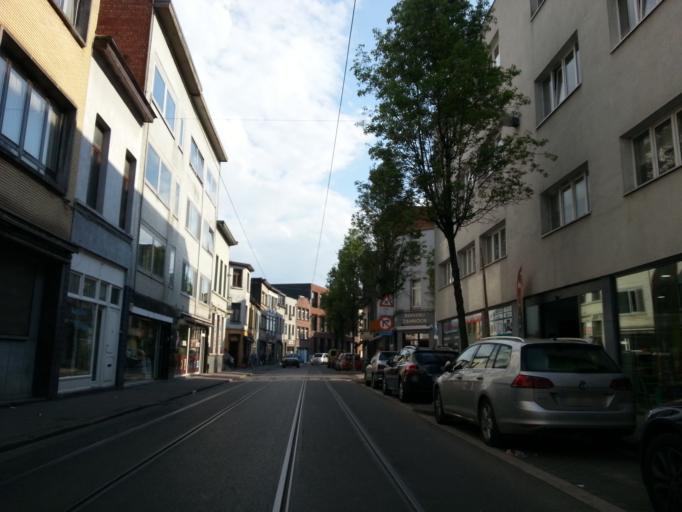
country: BE
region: Flanders
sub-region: Provincie Antwerpen
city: Antwerpen
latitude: 51.2123
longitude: 4.4261
